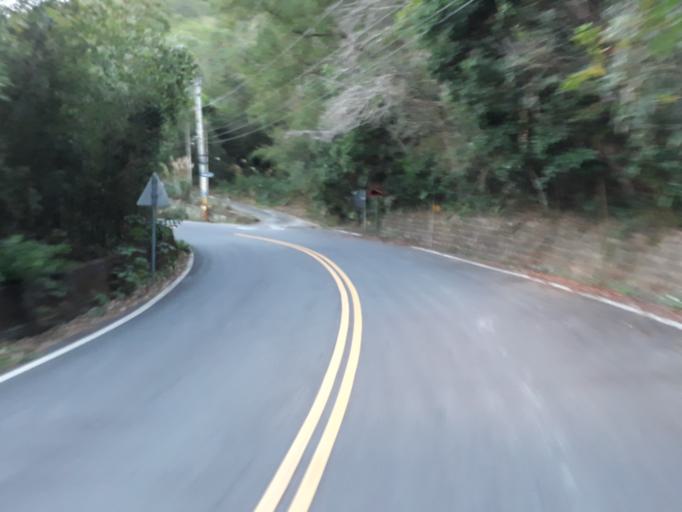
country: TW
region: Taiwan
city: Fengyuan
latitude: 24.3692
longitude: 120.8650
